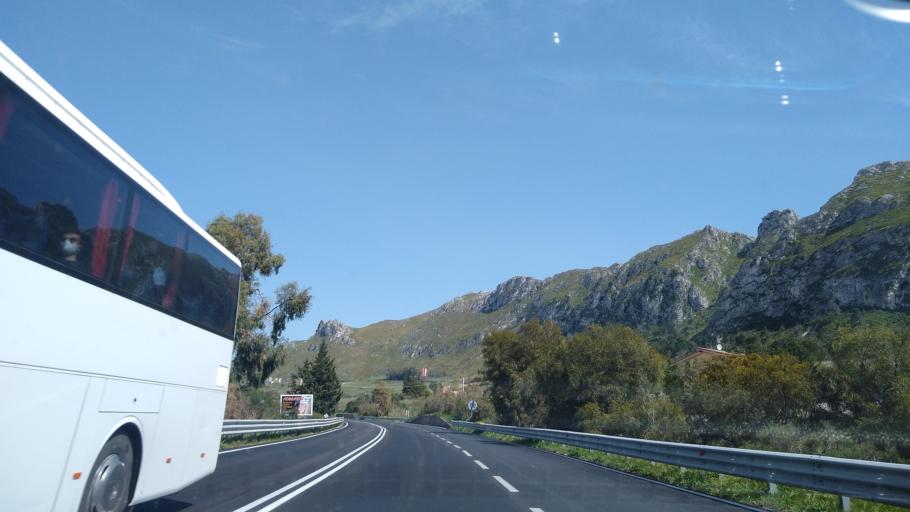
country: IT
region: Sicily
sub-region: Palermo
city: San Giuseppe Jato
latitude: 37.9749
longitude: 13.2061
